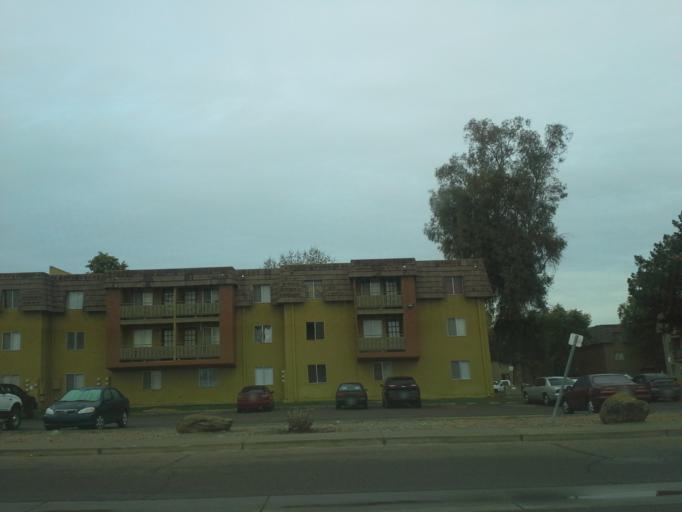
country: US
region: Arizona
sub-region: Maricopa County
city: Glendale
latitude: 33.6413
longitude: -112.0611
